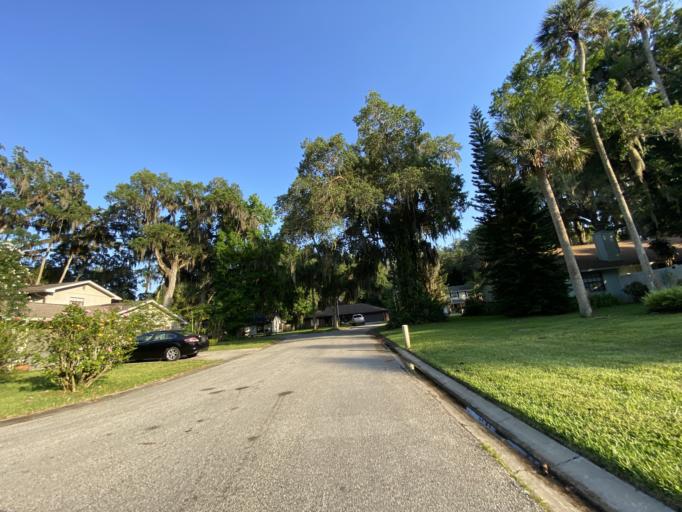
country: US
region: Florida
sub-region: Volusia County
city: Port Orange
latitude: 29.1473
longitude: -81.0061
